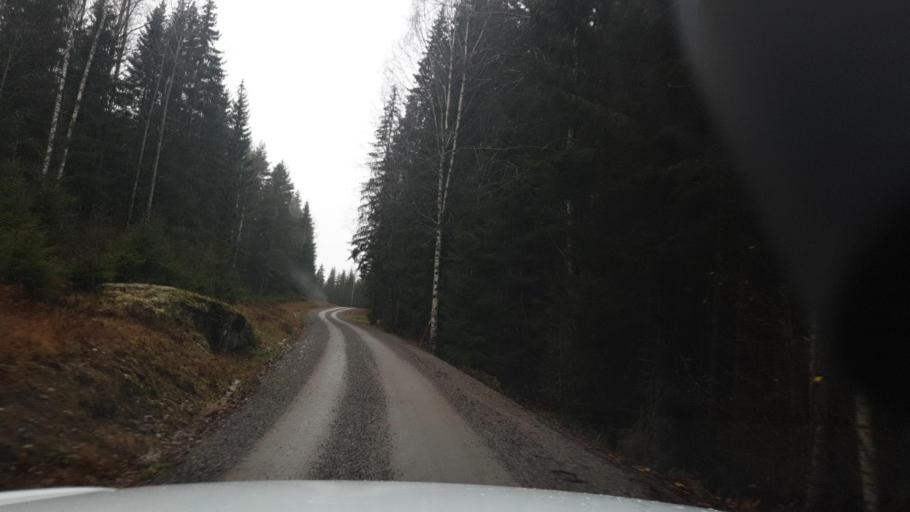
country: SE
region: Vaermland
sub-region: Arvika Kommun
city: Arvika
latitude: 59.5819
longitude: 12.8197
